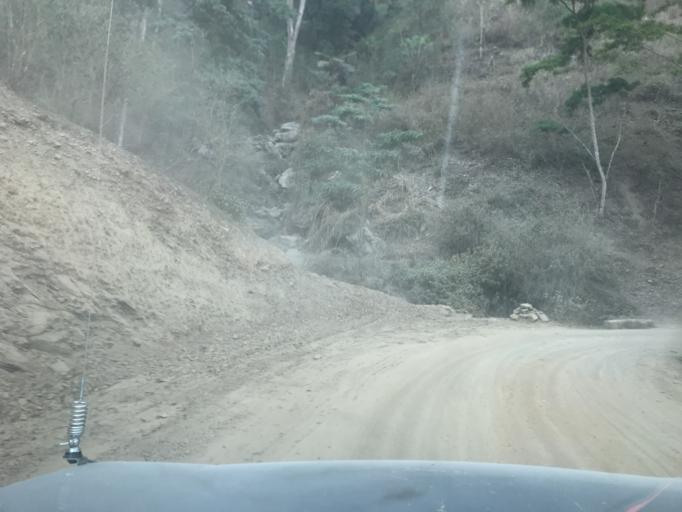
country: TL
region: Ermera
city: Gleno
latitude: -8.7639
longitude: 125.4353
